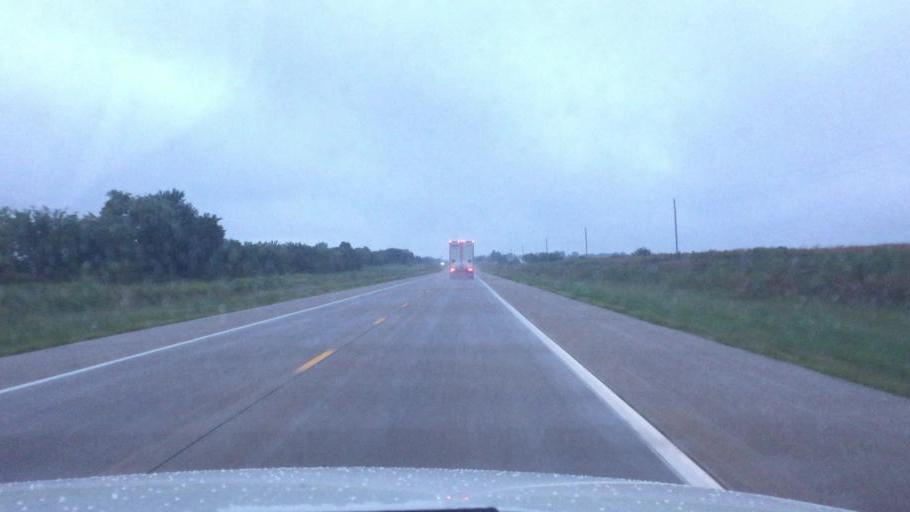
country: US
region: Kansas
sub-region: Neosho County
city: Chanute
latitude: 37.5105
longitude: -95.4709
